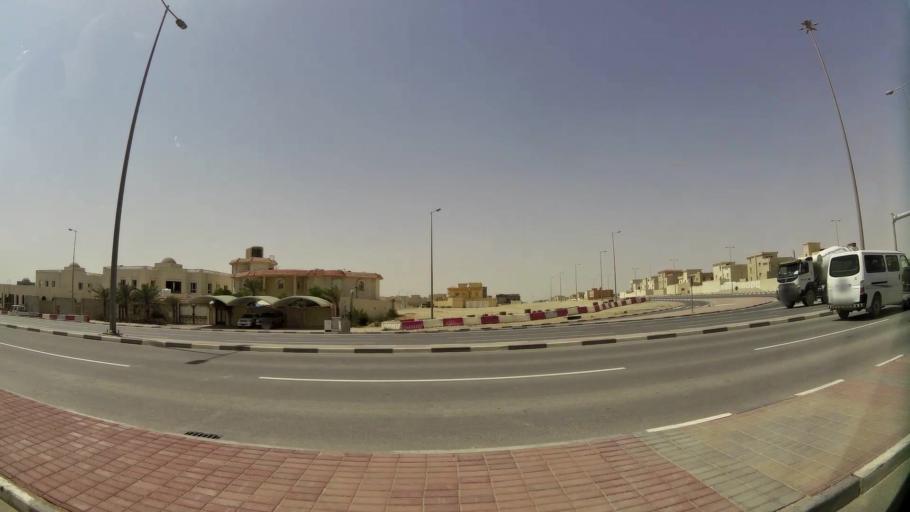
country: QA
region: Baladiyat Umm Salal
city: Umm Salal Muhammad
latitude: 25.4043
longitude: 51.4556
